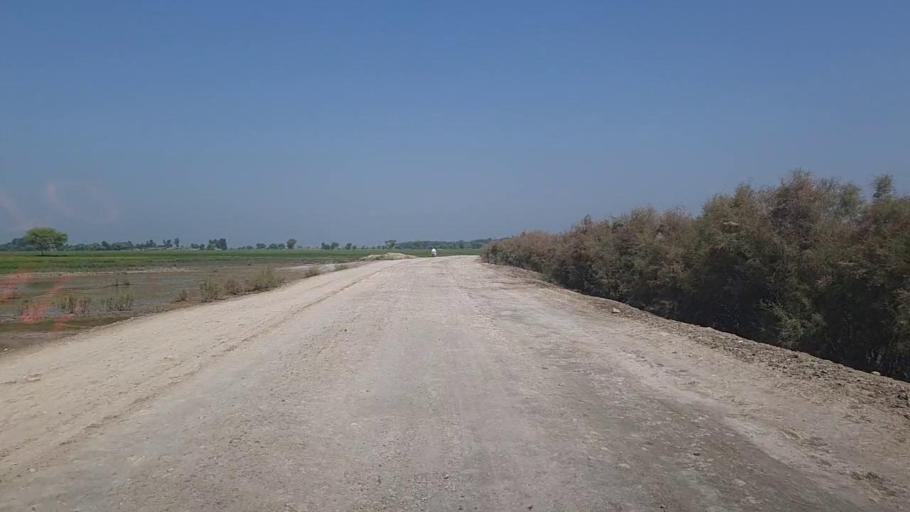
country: PK
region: Sindh
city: Kandhkot
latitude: 28.2997
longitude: 69.2910
